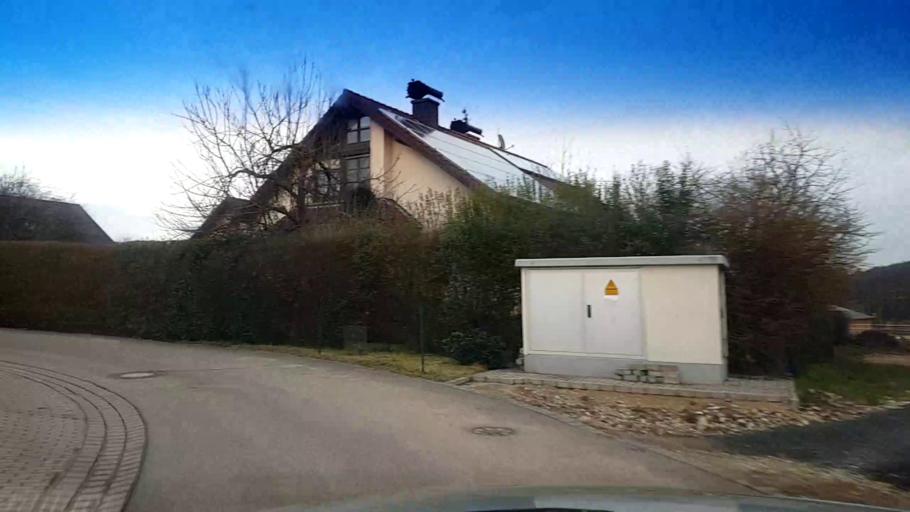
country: DE
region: Bavaria
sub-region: Upper Franconia
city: Pommersfelden
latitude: 49.8159
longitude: 10.8090
